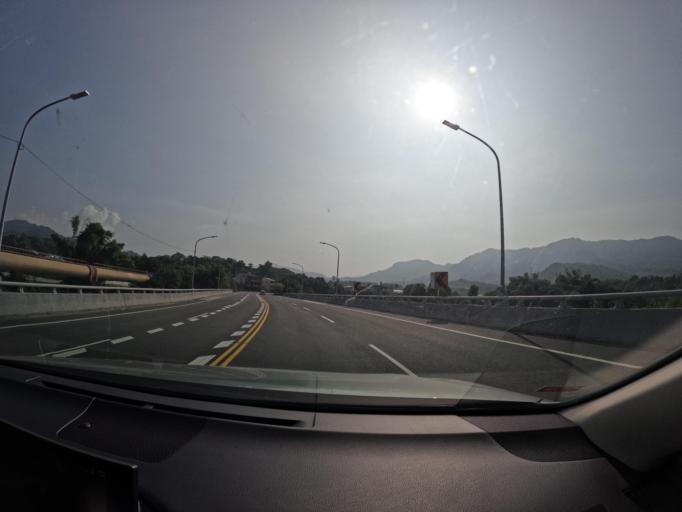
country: TW
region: Taiwan
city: Yujing
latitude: 23.0742
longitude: 120.4970
